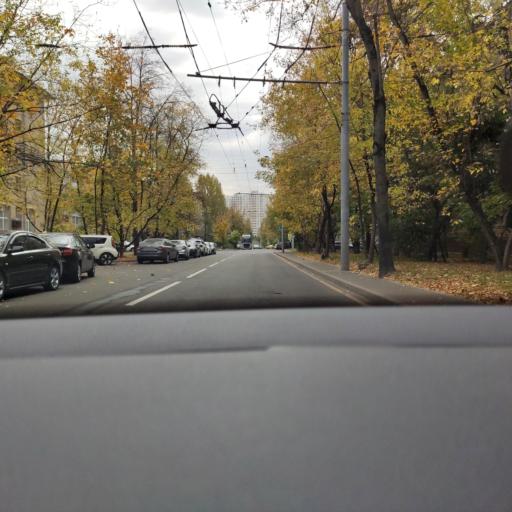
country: RU
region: Moscow
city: Novovladykino
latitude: 55.8333
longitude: 37.5918
